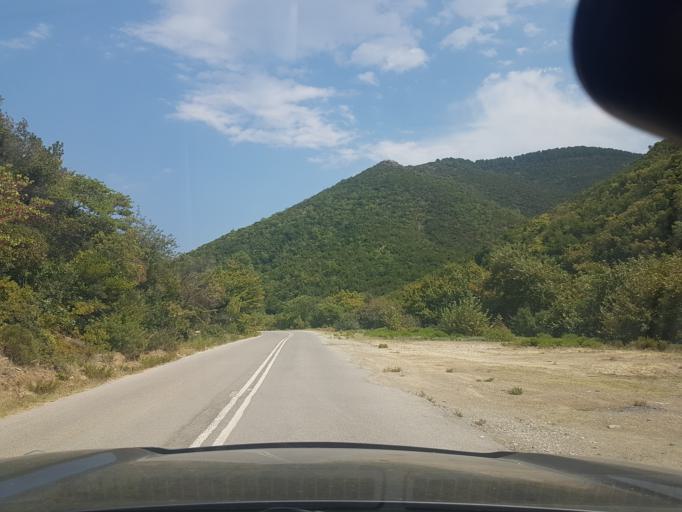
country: GR
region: Central Greece
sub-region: Nomos Evvoias
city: Kymi
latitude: 38.6375
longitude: 24.0796
